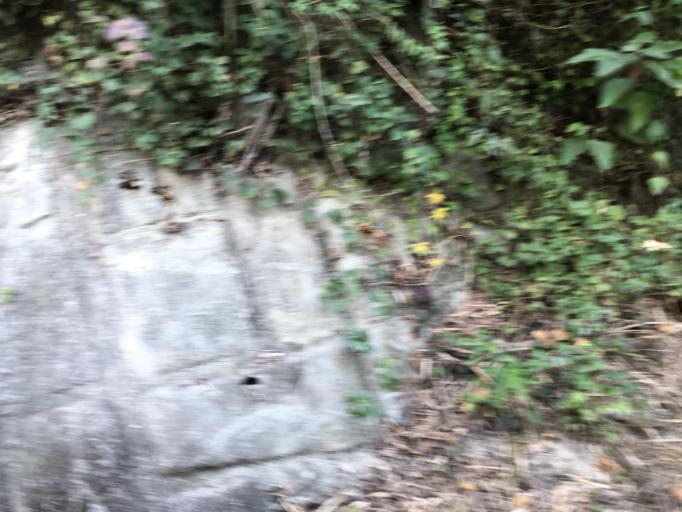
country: TW
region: Taiwan
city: Yujing
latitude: 23.0168
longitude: 120.3830
